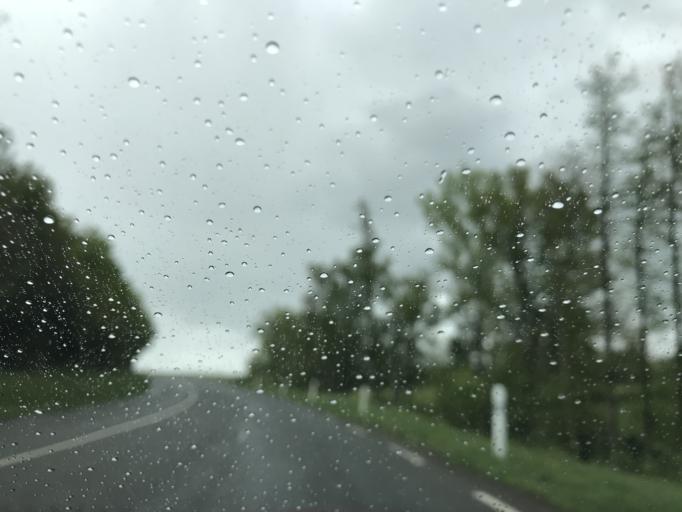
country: FR
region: Auvergne
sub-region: Departement du Puy-de-Dome
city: Billom
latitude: 45.7158
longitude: 3.3794
